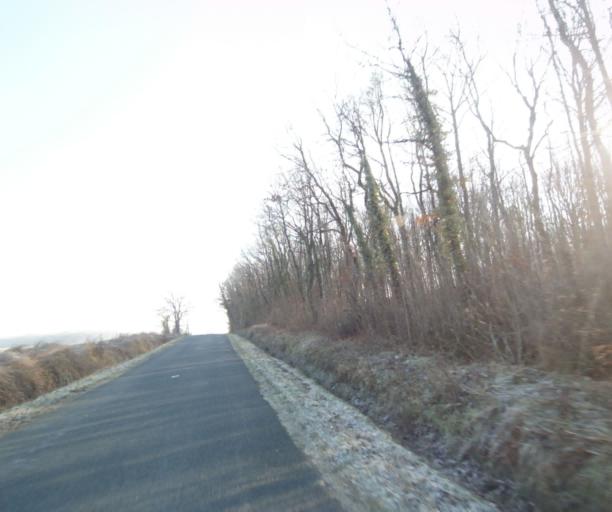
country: FR
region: Champagne-Ardenne
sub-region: Departement de la Haute-Marne
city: Chevillon
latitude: 48.4897
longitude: 5.0774
